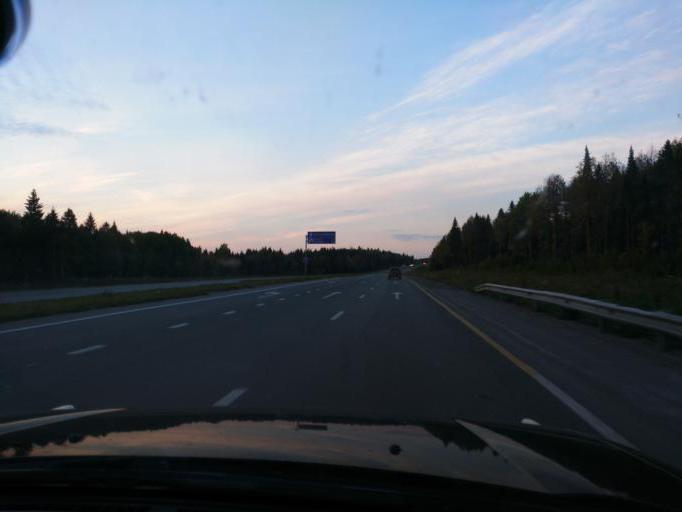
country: RU
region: Perm
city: Polazna
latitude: 58.2513
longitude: 56.4107
